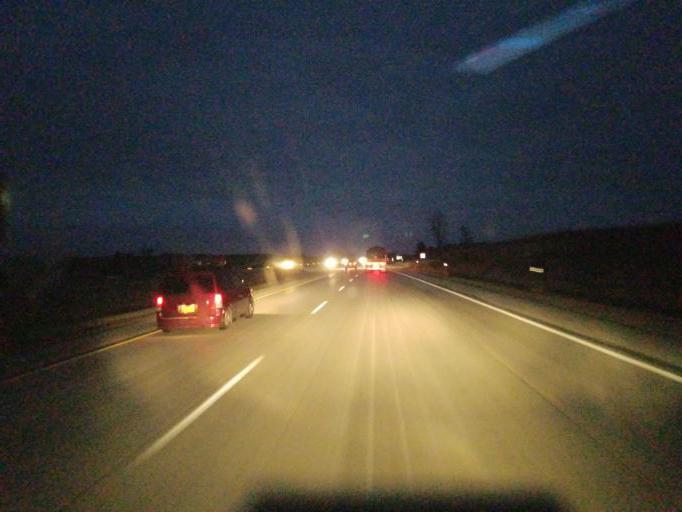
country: US
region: Iowa
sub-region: Guthrie County
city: Guthrie Center
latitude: 41.4966
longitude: -94.5565
